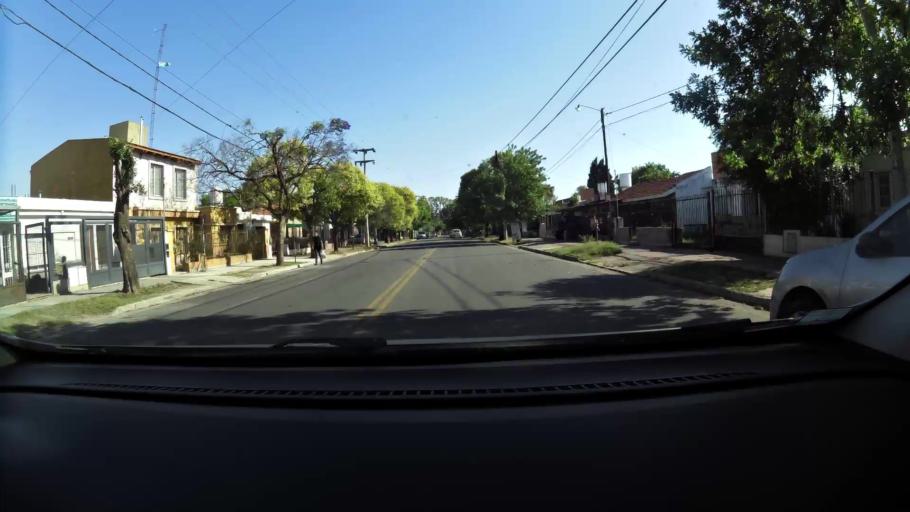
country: AR
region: Cordoba
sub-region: Departamento de Capital
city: Cordoba
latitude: -31.3651
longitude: -64.2126
